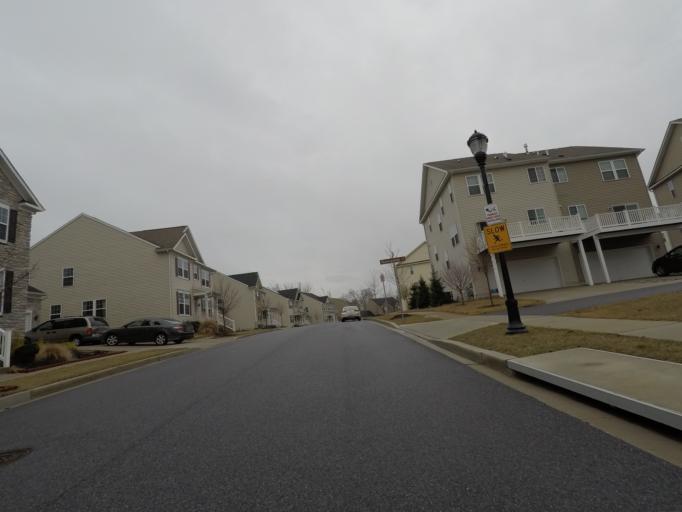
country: US
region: Maryland
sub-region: Howard County
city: Ellicott City
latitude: 39.2920
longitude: -76.8120
